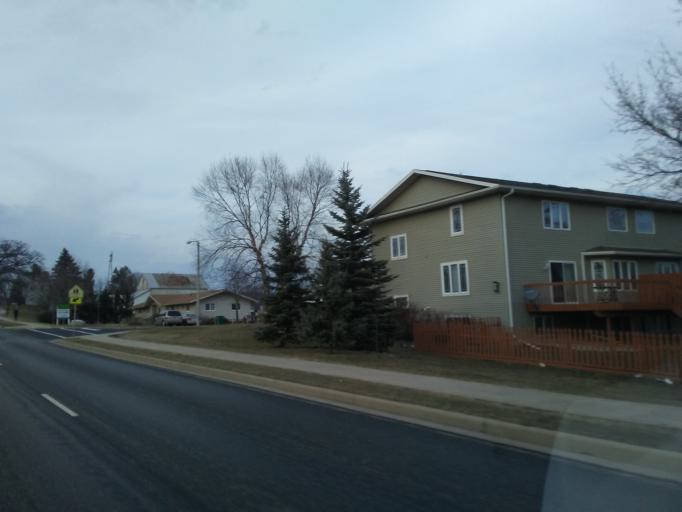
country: US
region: Wisconsin
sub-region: Dane County
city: Verona
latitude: 42.9987
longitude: -89.5337
